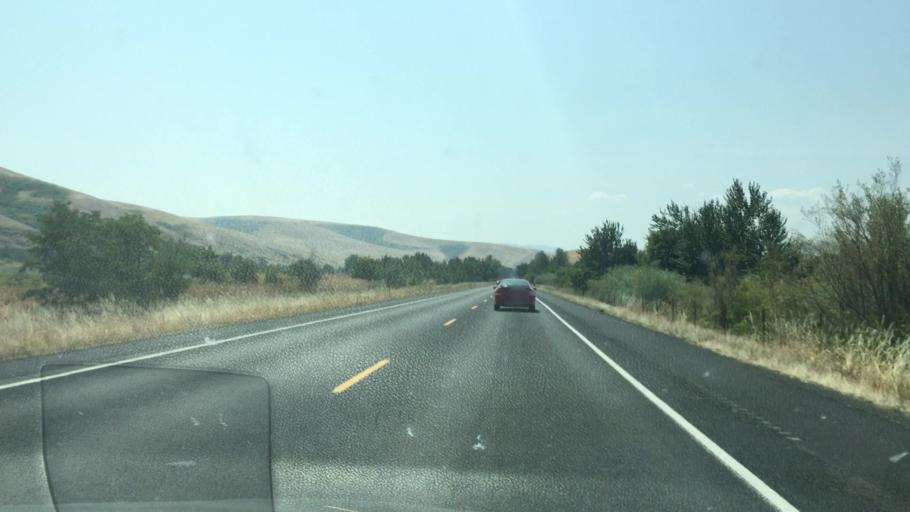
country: US
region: Idaho
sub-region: Nez Perce County
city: Lapwai
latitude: 46.4334
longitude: -116.8078
